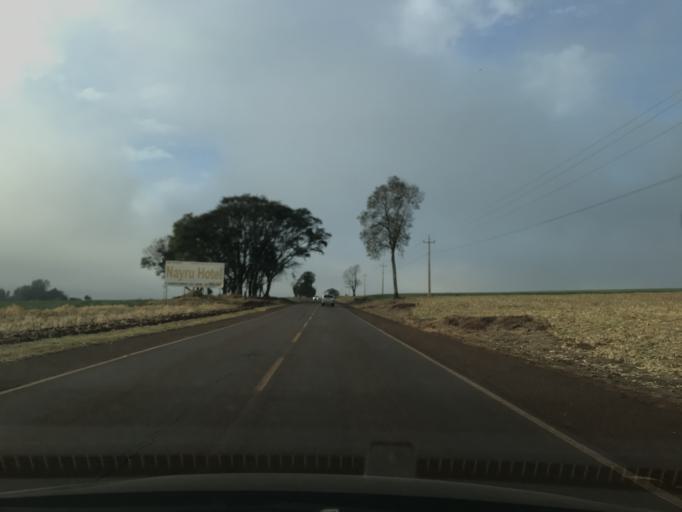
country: BR
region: Parana
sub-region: Toledo
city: Toledo
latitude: -24.6534
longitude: -53.7056
